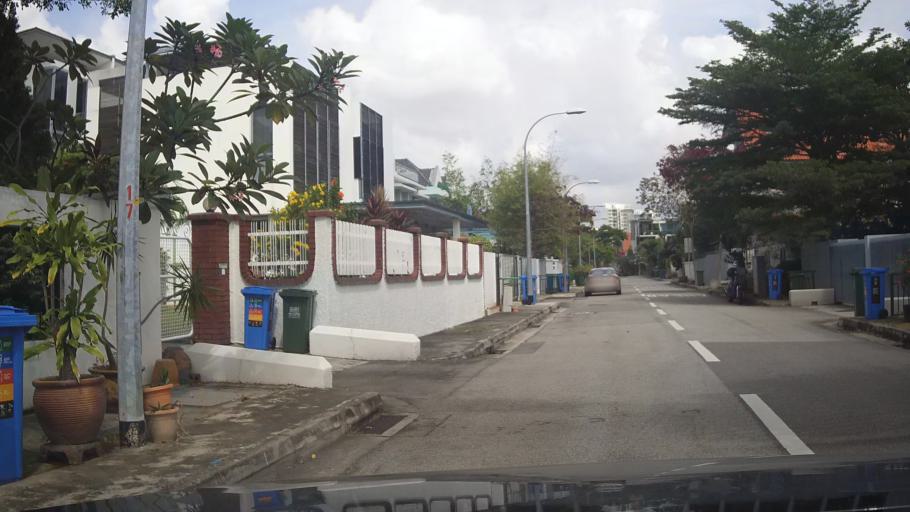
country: SG
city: Singapore
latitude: 1.3135
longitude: 103.9163
